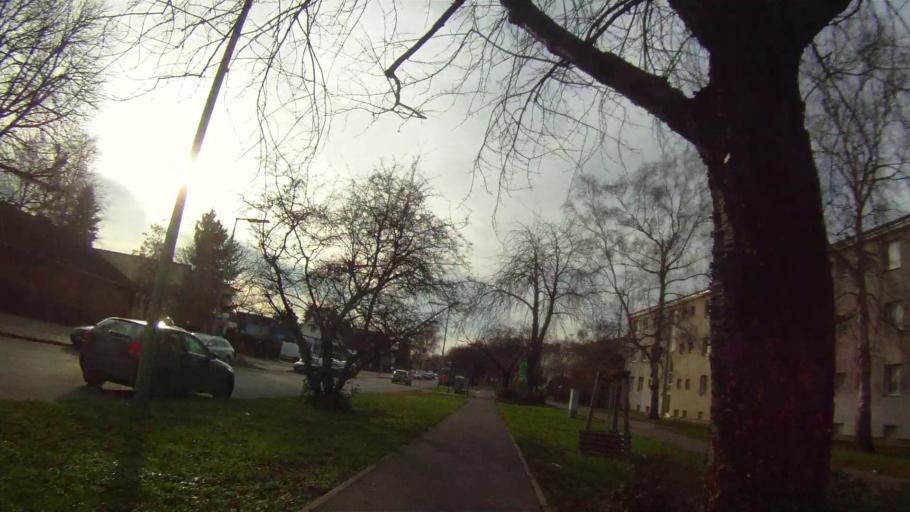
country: DE
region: Berlin
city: Buckow
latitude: 52.4403
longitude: 13.4536
